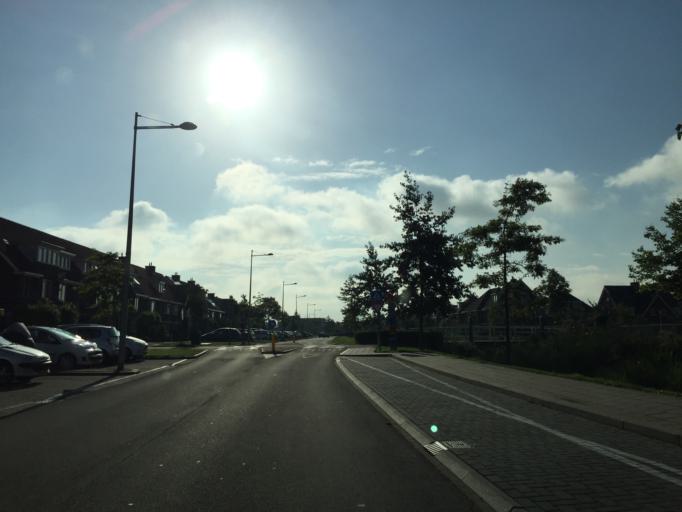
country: NL
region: South Holland
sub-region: Gemeente Lansingerland
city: Berkel en Rodenrijs
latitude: 51.9898
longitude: 4.4582
